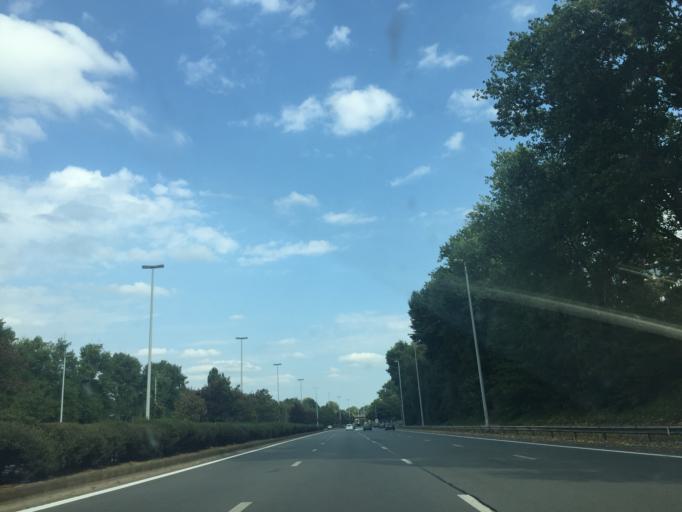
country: BE
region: Flanders
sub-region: Provincie Vlaams-Brabant
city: Diegem
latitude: 50.8554
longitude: 4.4199
